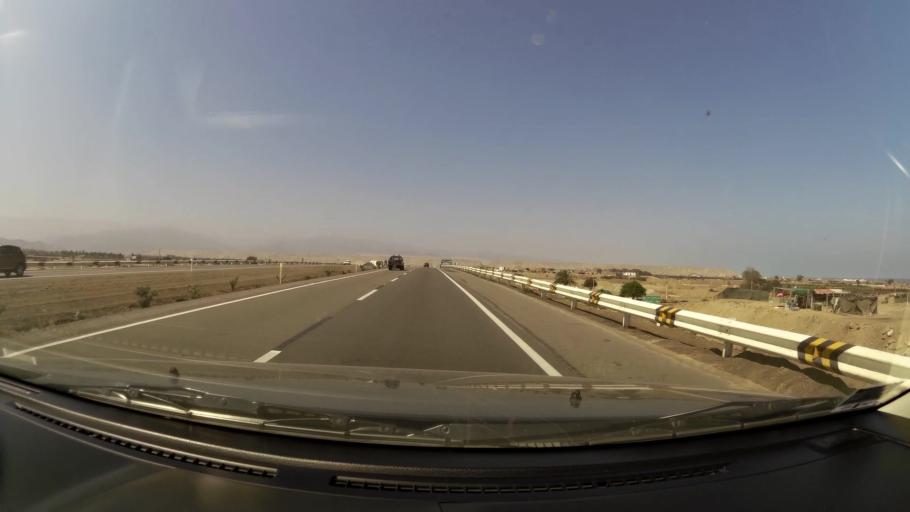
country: PE
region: Lima
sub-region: Provincia de Canete
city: Asia
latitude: -12.7863
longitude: -76.5726
